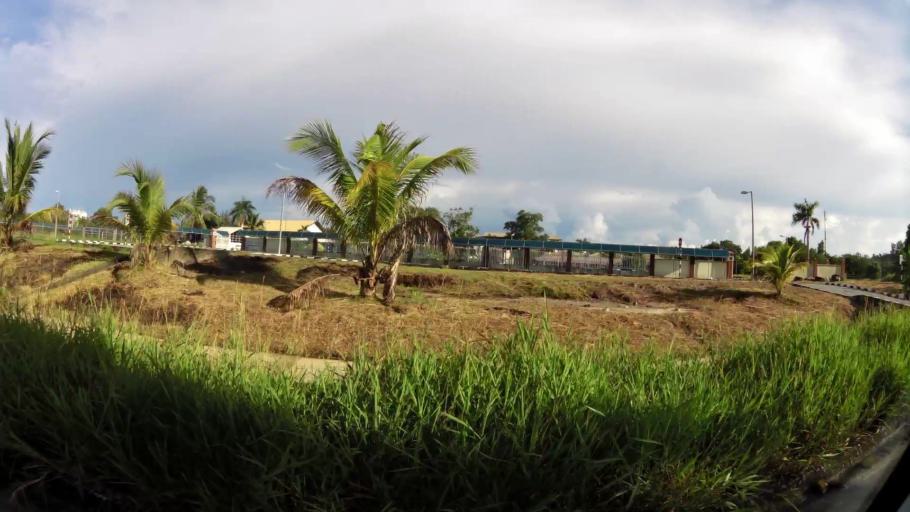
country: BN
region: Brunei and Muara
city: Bandar Seri Begawan
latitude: 4.9835
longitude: 114.9696
